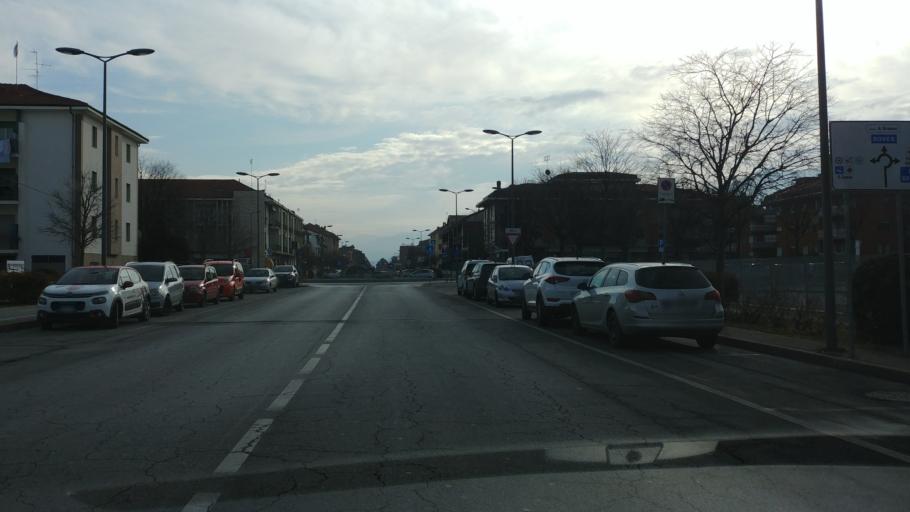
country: IT
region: Piedmont
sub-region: Provincia di Cuneo
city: Cuneo
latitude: 44.3804
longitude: 7.5288
